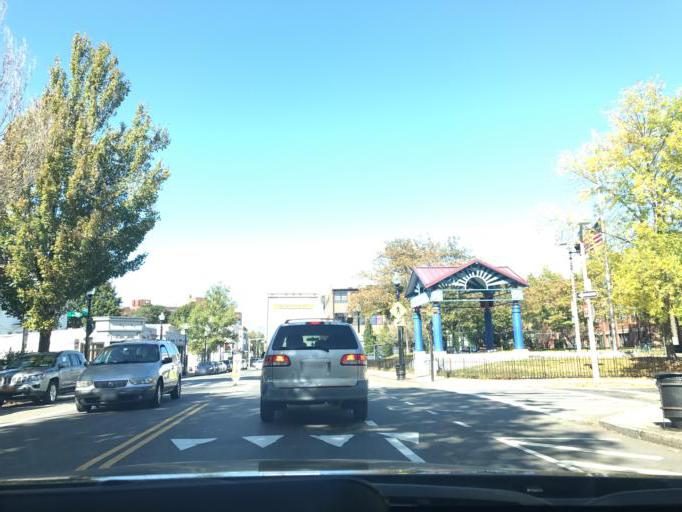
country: US
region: Massachusetts
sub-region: Suffolk County
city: South Boston
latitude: 42.3174
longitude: -71.0566
